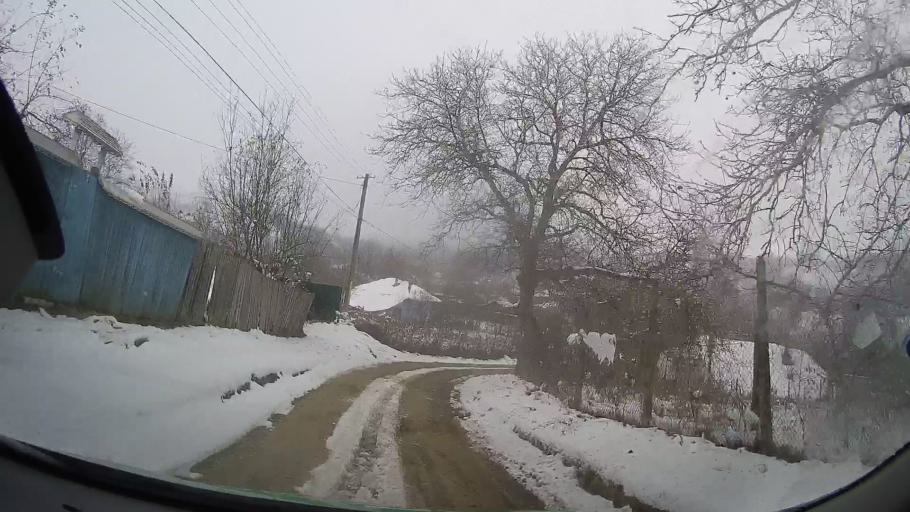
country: RO
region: Bacau
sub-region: Comuna Vultureni
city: Vultureni
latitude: 46.3778
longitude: 27.2848
